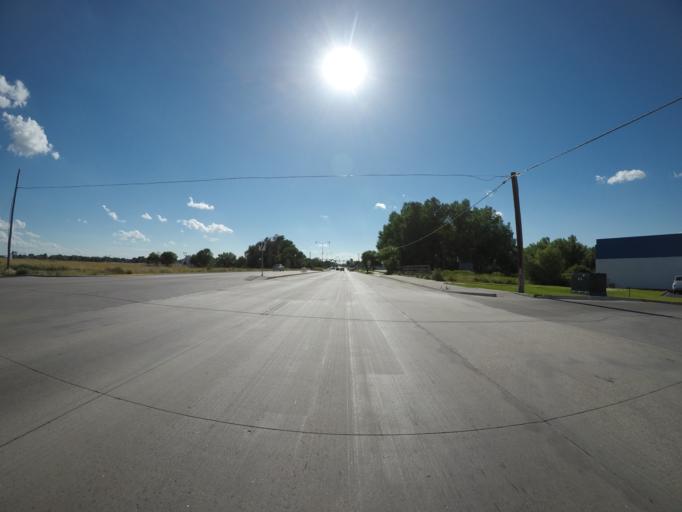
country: US
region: Colorado
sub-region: Logan County
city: Sterling
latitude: 40.6252
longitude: -103.2328
